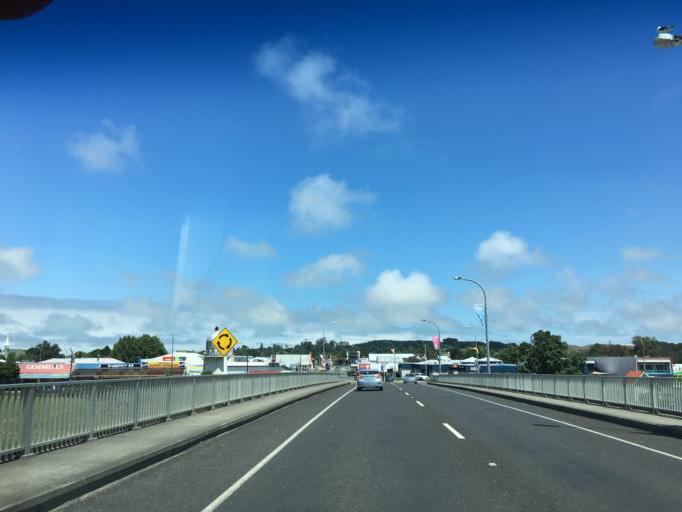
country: NZ
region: Hawke's Bay
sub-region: Wairoa District
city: Wairoa
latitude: -39.0319
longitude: 177.4187
